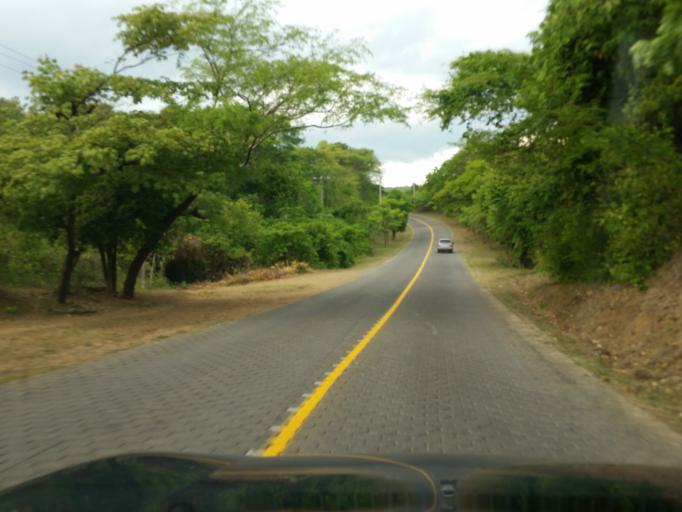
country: NI
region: Managua
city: Masachapa
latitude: 11.8607
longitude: -86.5190
